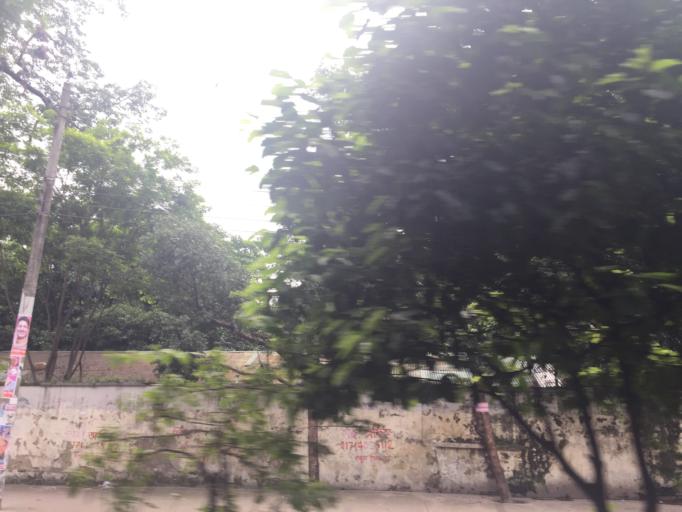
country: BD
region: Dhaka
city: Paltan
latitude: 23.7272
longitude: 90.4043
